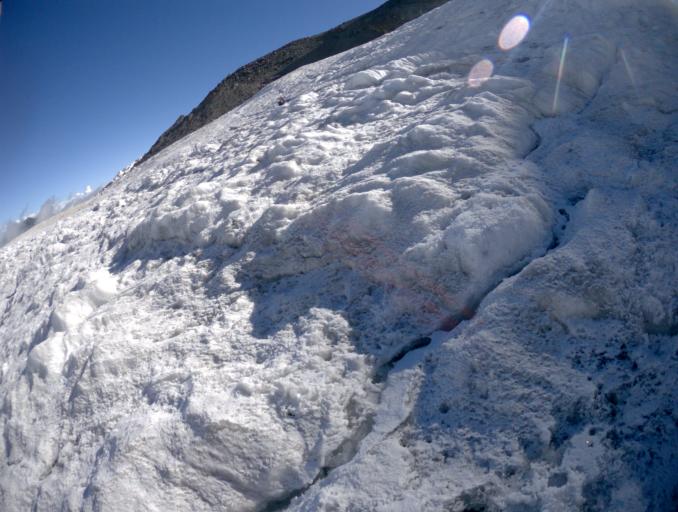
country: RU
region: Kabardino-Balkariya
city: Terskol
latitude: 43.3871
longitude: 42.4334
